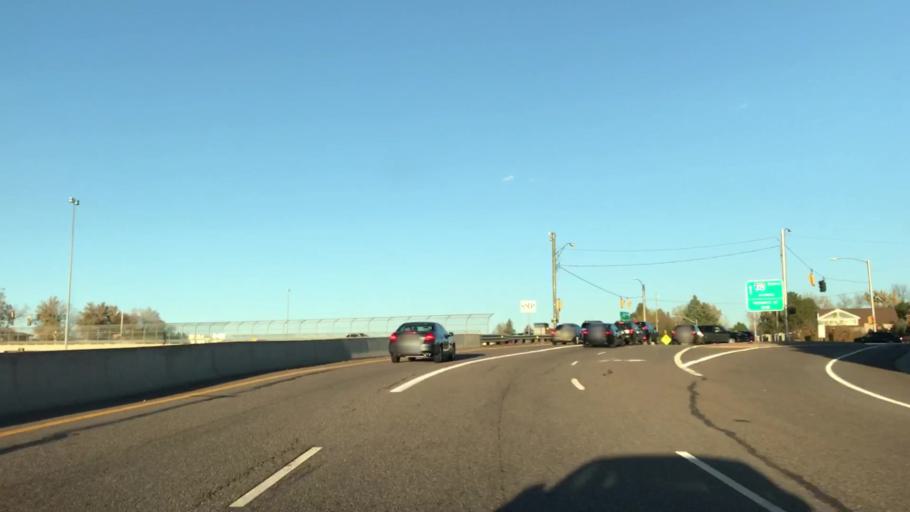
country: US
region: Colorado
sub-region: Arapahoe County
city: Castlewood
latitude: 39.6386
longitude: -104.8861
